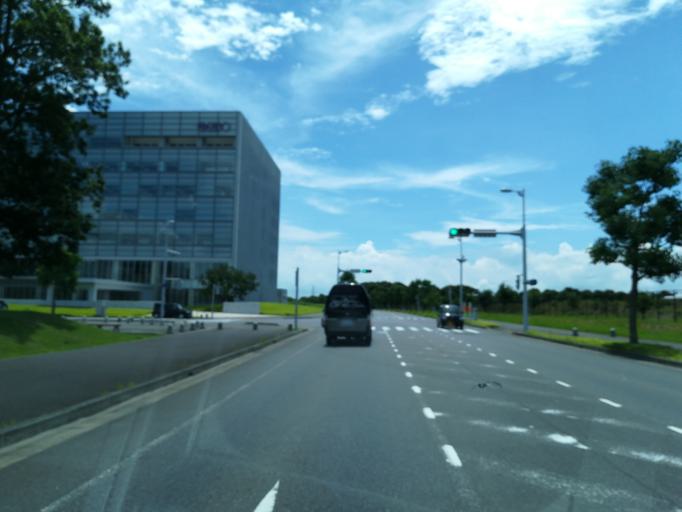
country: JP
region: Ibaraki
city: Naka
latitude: 36.0801
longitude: 140.0793
